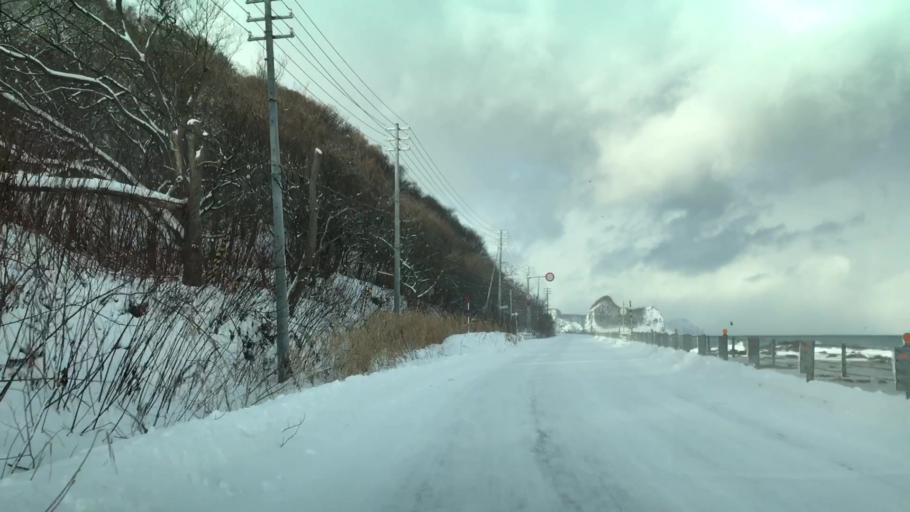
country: JP
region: Hokkaido
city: Yoichi
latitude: 43.2948
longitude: 140.6229
